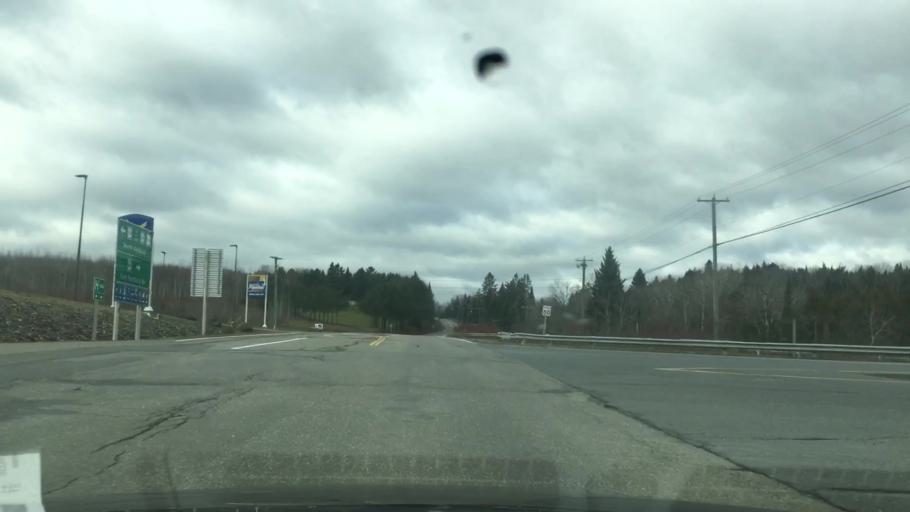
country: US
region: Maine
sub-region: Aroostook County
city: Fort Fairfield
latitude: 46.7495
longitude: -67.7184
